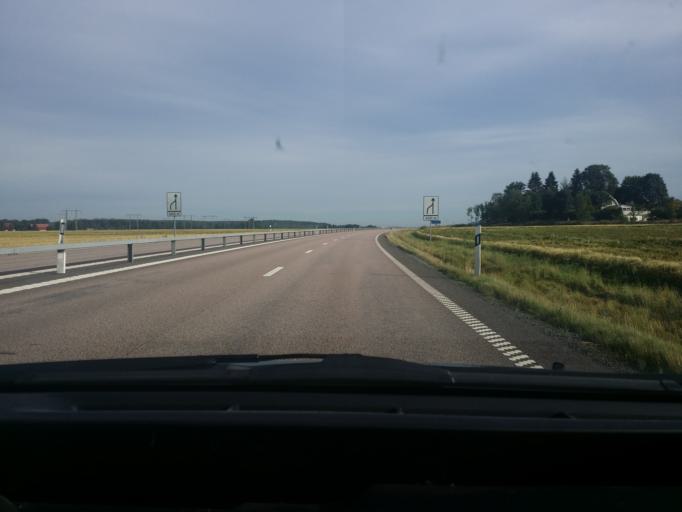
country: SE
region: Vaestmanland
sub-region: Vasteras
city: Hokasen
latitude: 59.7487
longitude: 16.5557
